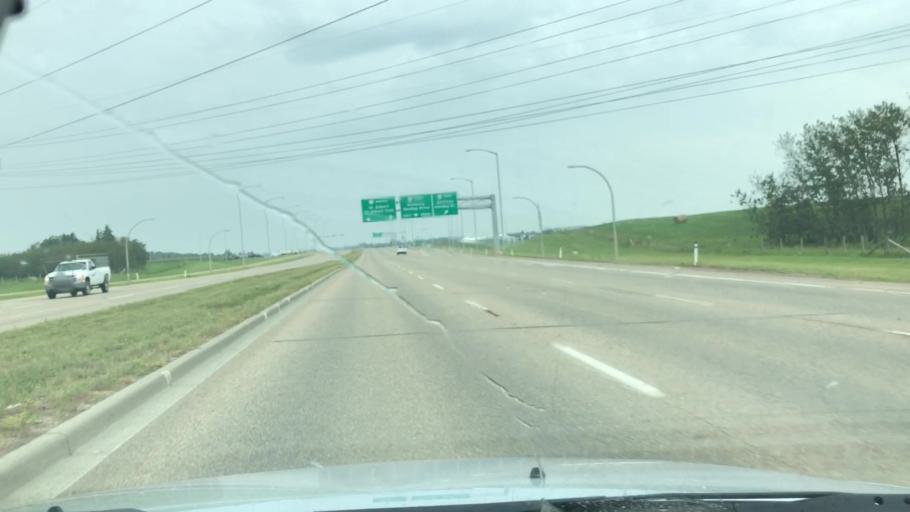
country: CA
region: Alberta
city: St. Albert
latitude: 53.6134
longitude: -113.5942
